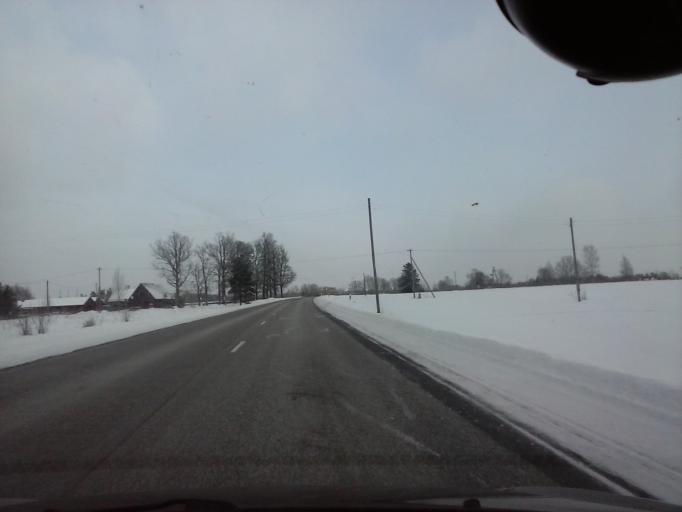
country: EE
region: Paernumaa
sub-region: Saarde vald
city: Kilingi-Nomme
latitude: 58.1760
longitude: 25.0381
